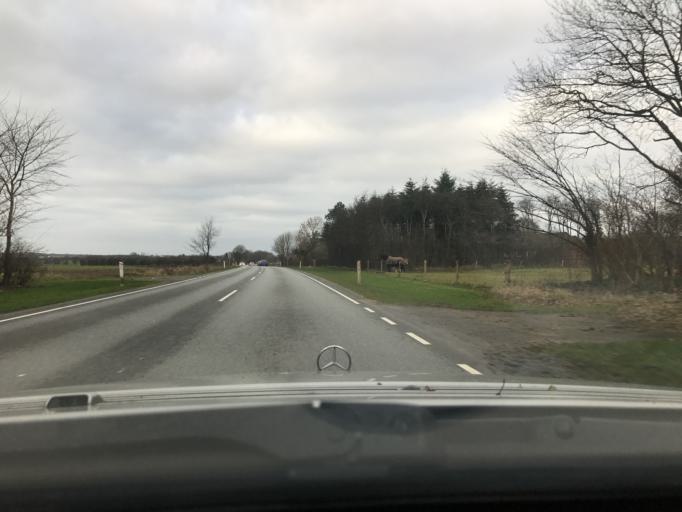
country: DK
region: South Denmark
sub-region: Aabenraa Kommune
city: Rodekro
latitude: 55.0906
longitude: 9.2032
